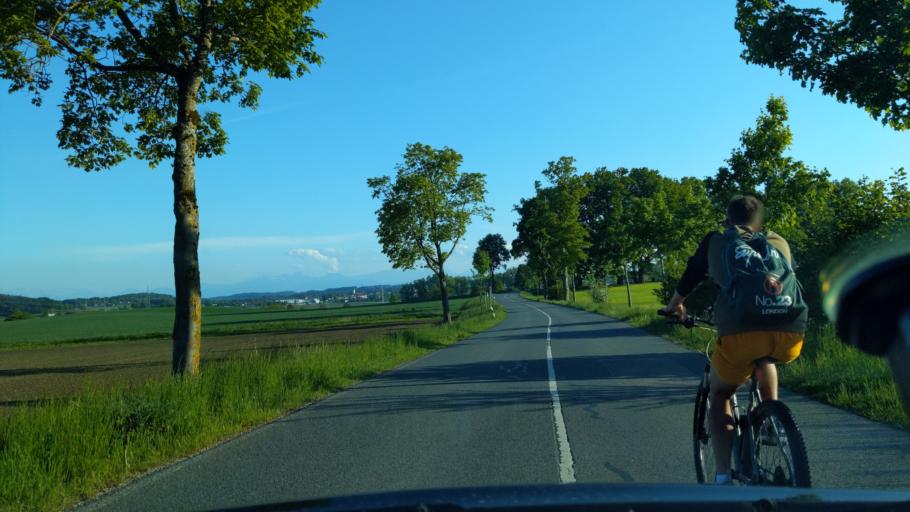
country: DE
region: Bavaria
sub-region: Upper Bavaria
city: Ebersberg
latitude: 48.0686
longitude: 11.9692
